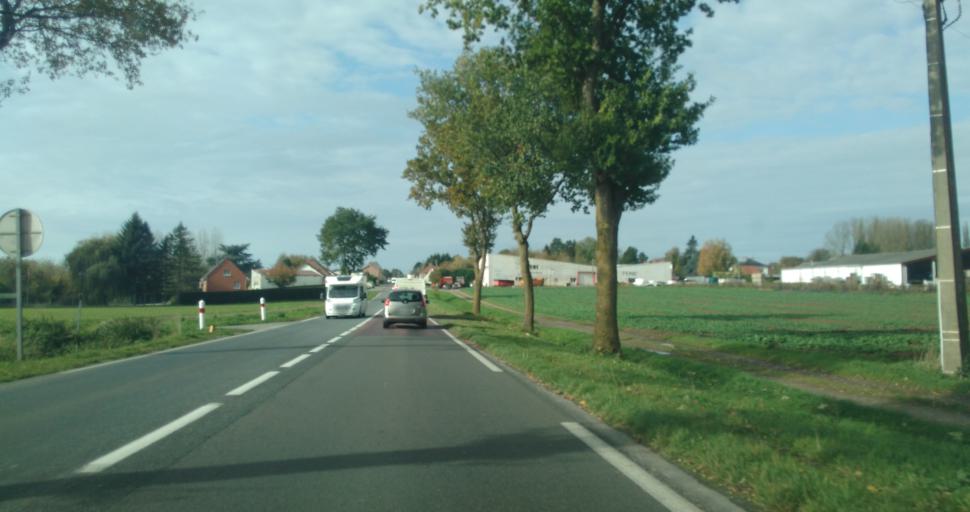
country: FR
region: Nord-Pas-de-Calais
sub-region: Departement du Pas-de-Calais
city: Savy-Berlette
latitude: 50.3531
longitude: 2.4971
